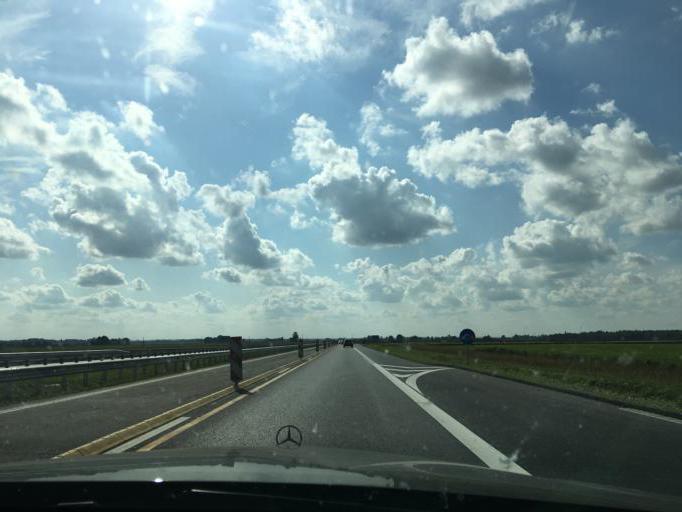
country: LT
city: Kazlu Ruda
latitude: 54.6660
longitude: 23.5146
